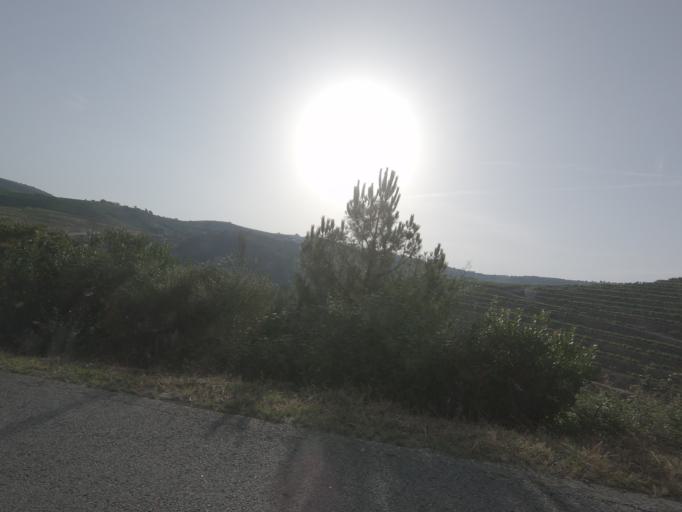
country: PT
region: Vila Real
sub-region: Sabrosa
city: Sabrosa
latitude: 41.2213
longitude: -7.5128
